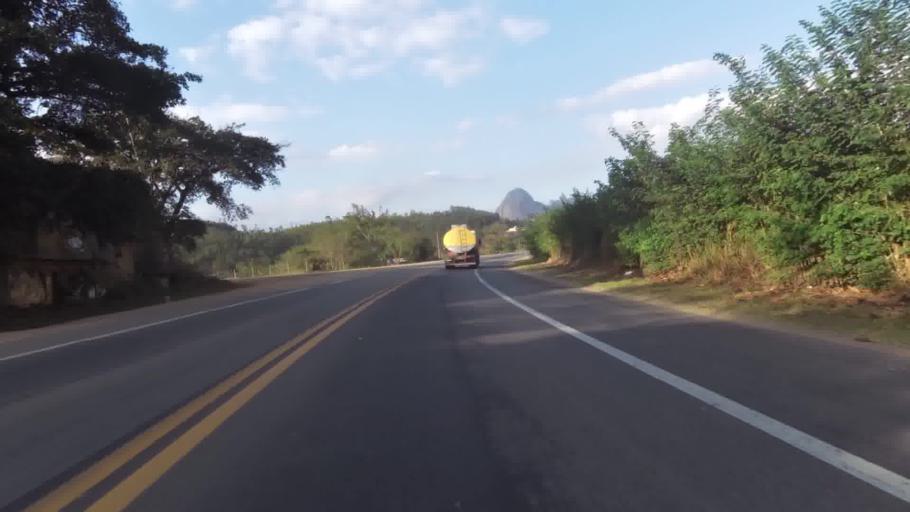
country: BR
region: Espirito Santo
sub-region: Cachoeiro De Itapemirim
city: Cachoeiro de Itapemirim
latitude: -20.9004
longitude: -41.0570
